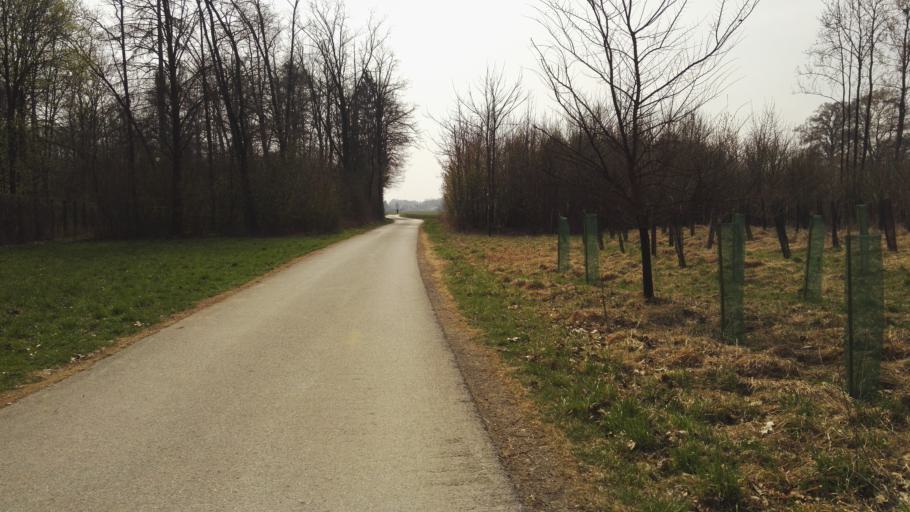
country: AT
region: Styria
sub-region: Politischer Bezirk Graz-Umgebung
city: Feldkirchen bei Graz
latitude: 47.0115
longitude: 15.4547
